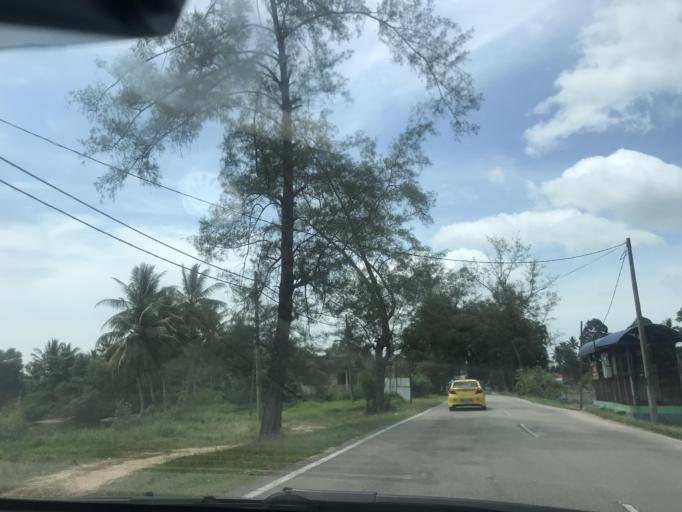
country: MY
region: Kelantan
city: Tumpat
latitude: 6.2120
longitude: 102.1315
